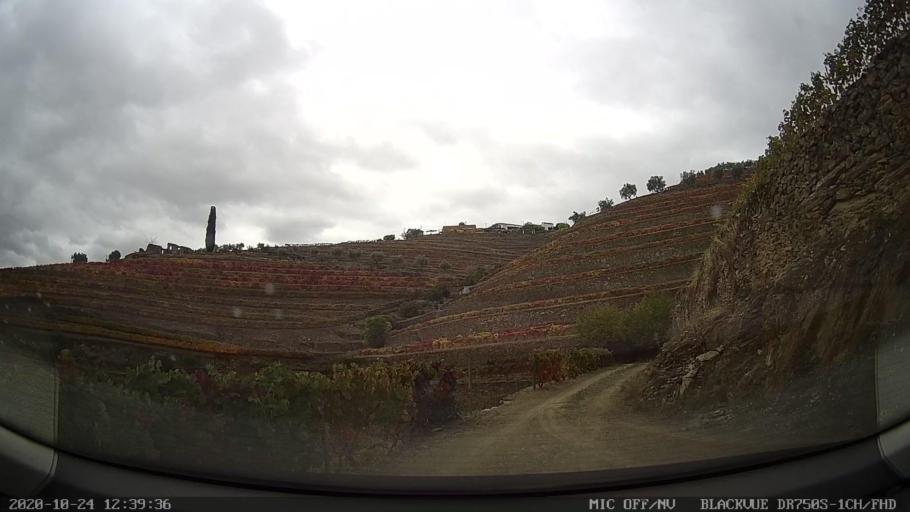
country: PT
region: Vila Real
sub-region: Sabrosa
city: Vilela
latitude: 41.1966
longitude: -7.5520
